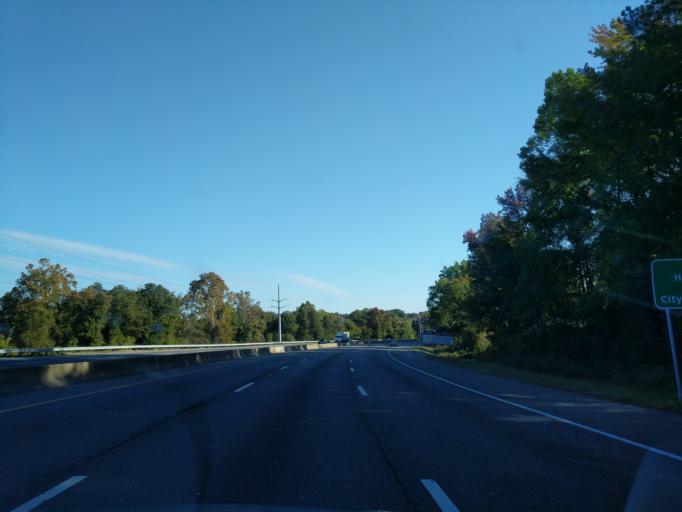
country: US
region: Virginia
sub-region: Henrico County
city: Lakeside
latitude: 37.5956
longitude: -77.4665
